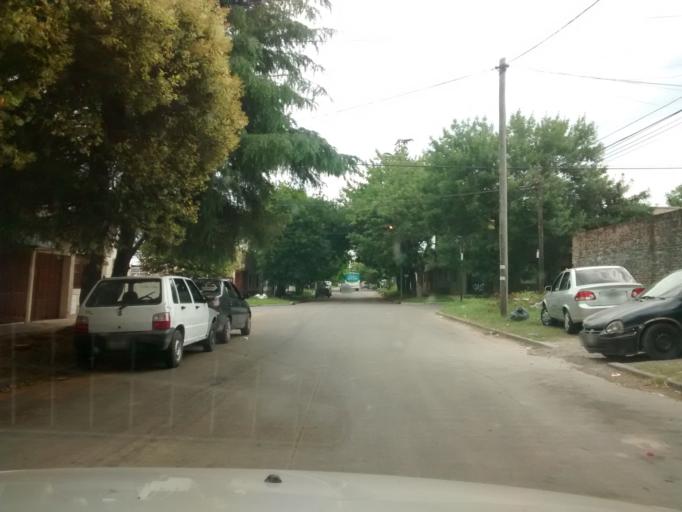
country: AR
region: Buenos Aires
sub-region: Partido de La Plata
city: La Plata
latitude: -34.9344
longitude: -57.9274
